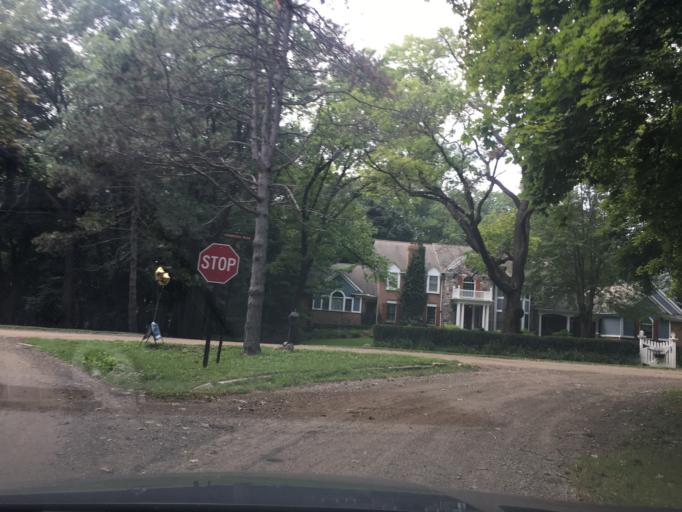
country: US
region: Michigan
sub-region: Oakland County
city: Bloomfield Hills
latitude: 42.5777
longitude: -83.2338
